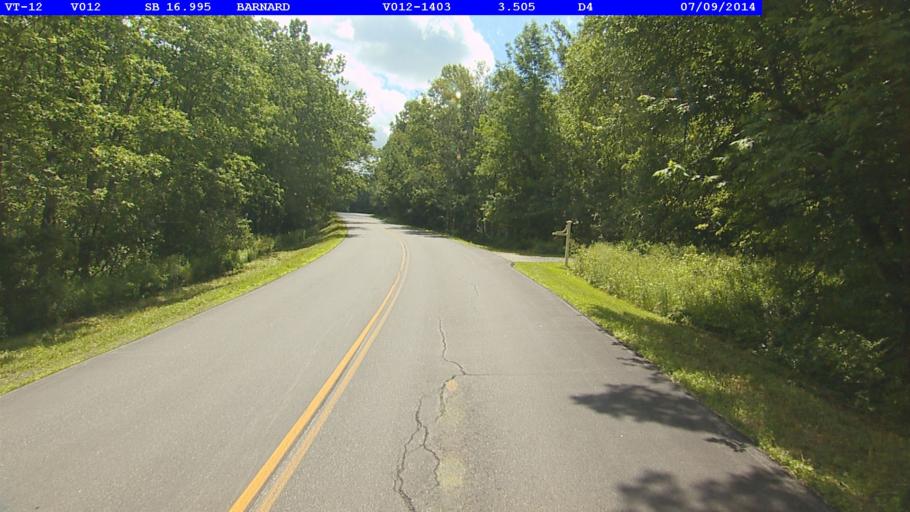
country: US
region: Vermont
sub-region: Windsor County
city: Woodstock
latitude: 43.7114
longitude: -72.6223
